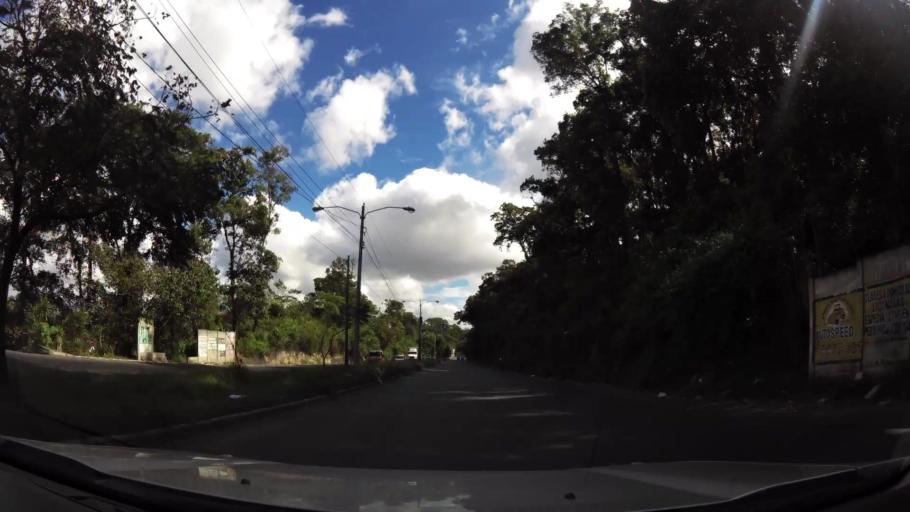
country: GT
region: Guatemala
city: Guatemala City
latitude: 14.6573
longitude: -90.5507
